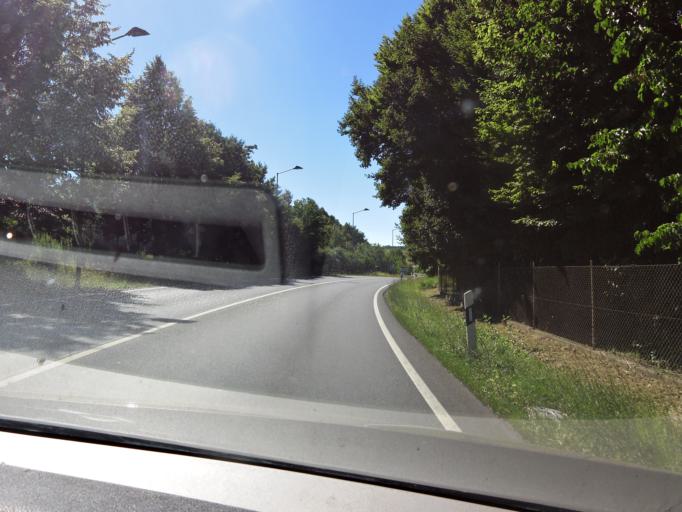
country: DE
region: Bavaria
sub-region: Regierungsbezirk Unterfranken
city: Kitzingen
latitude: 49.7405
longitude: 10.1432
